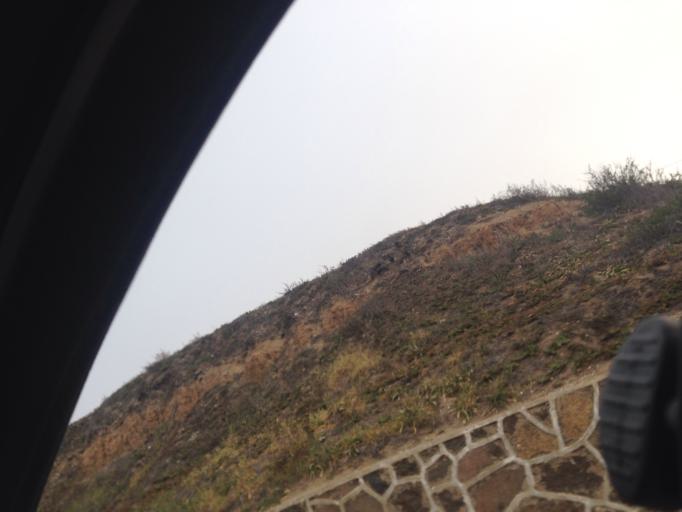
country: MX
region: Baja California
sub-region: Playas de Rosarito
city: Santa Anita
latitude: 32.0587
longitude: -116.8767
